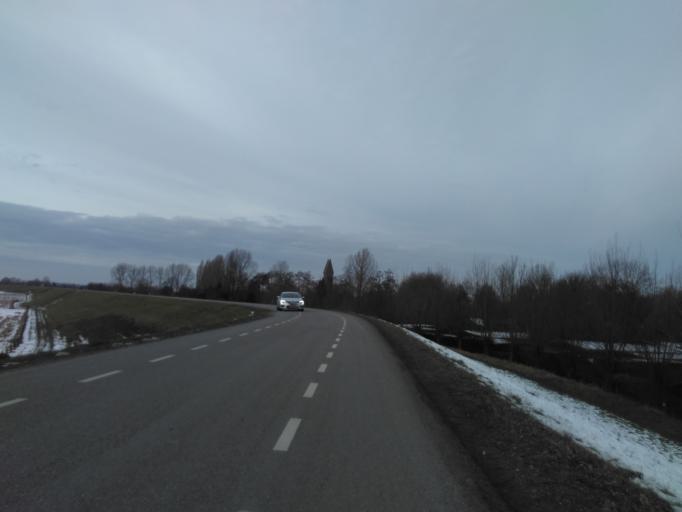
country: NL
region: Gelderland
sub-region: Gemeente Overbetuwe
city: Oosterhout
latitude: 51.8747
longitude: 5.8307
